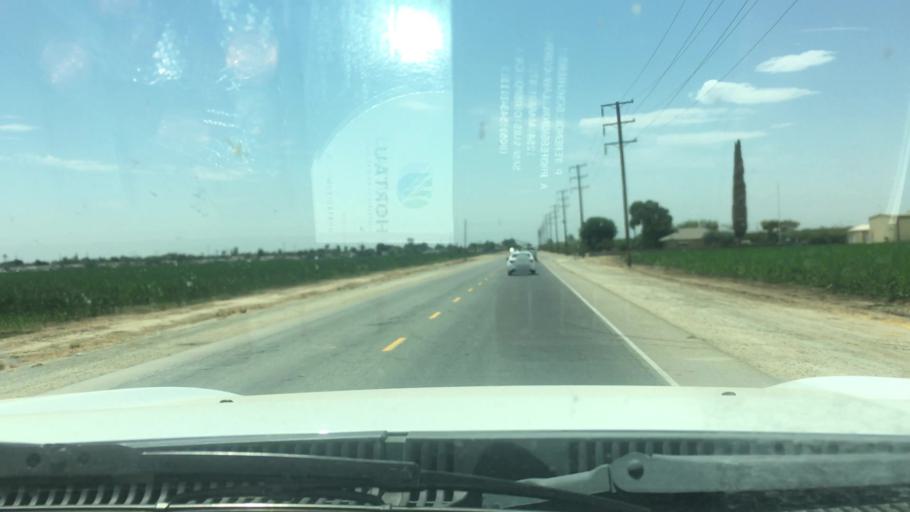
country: US
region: California
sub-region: Tulare County
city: Tipton
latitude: 36.0657
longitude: -119.2940
